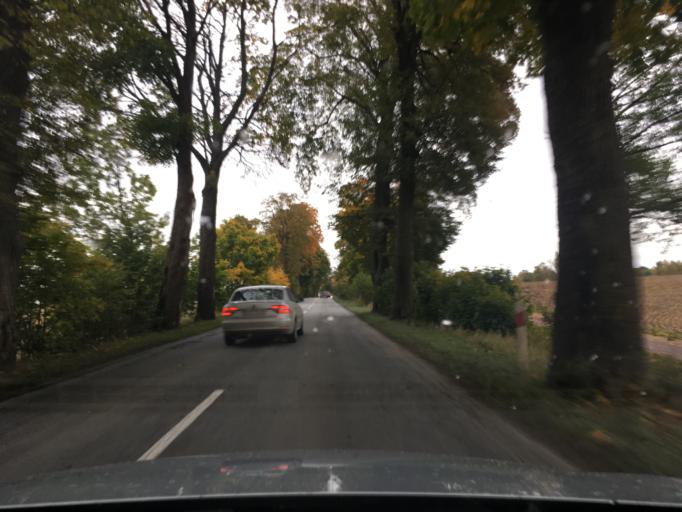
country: PL
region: Pomeranian Voivodeship
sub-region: Powiat koscierski
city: Grabowo Koscierskie
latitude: 54.1297
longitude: 18.1883
